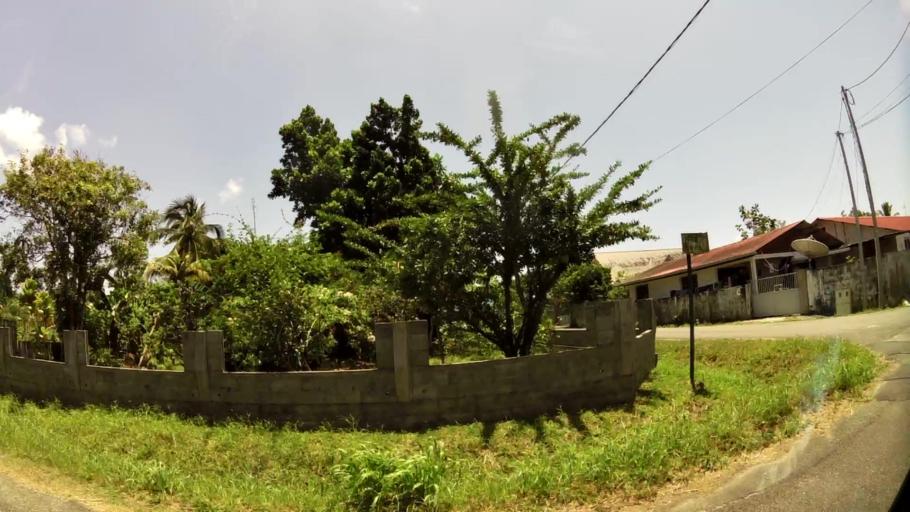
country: GF
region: Guyane
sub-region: Guyane
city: Matoury
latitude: 4.8855
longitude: -52.3392
